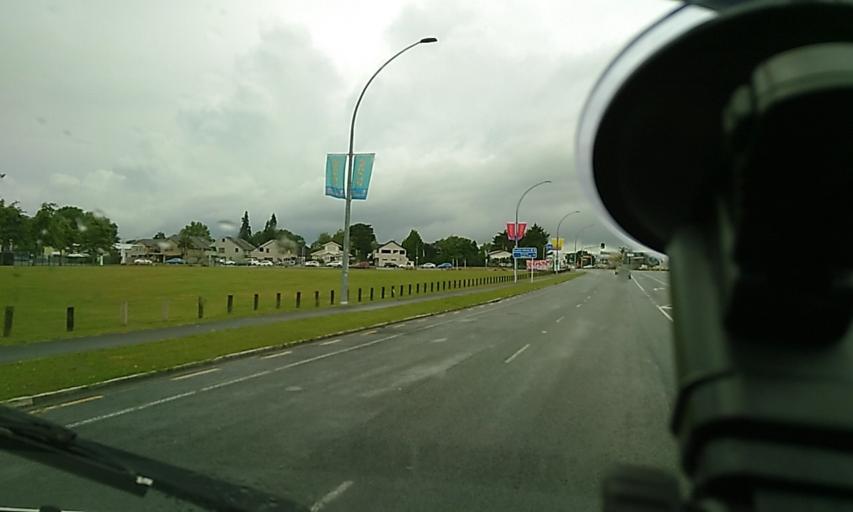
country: NZ
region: Waikato
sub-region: Hamilton City
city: Hamilton
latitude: -37.7825
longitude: 175.2696
